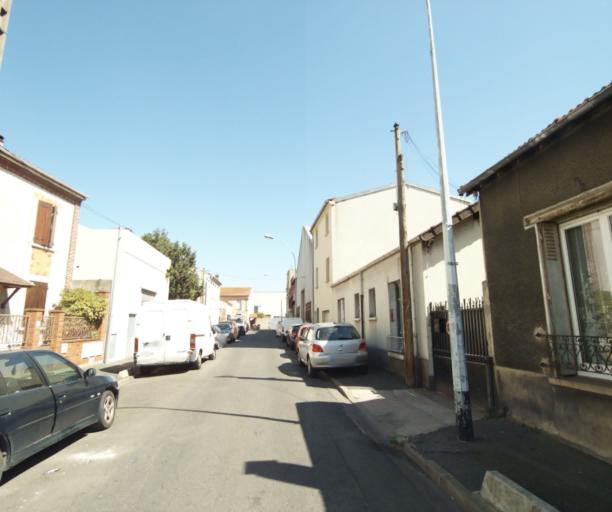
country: FR
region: Ile-de-France
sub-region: Departement de Seine-Saint-Denis
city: Saint-Denis
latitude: 48.9251
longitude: 2.3458
